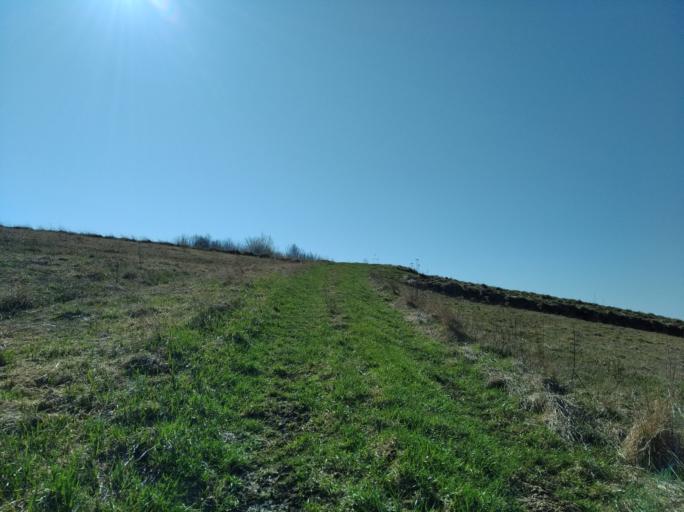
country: PL
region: Subcarpathian Voivodeship
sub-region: Powiat strzyzowski
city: Strzyzow
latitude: 49.8287
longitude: 21.8361
